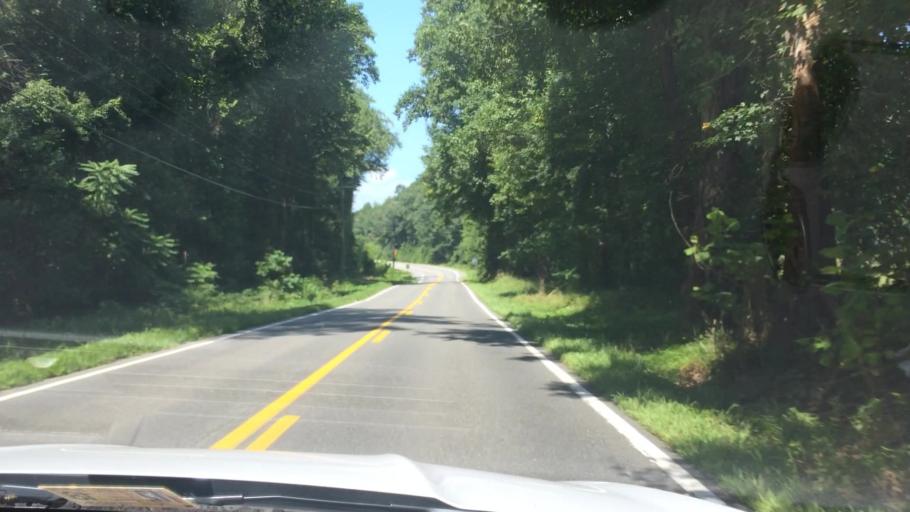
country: US
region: Virginia
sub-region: New Kent County
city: New Kent
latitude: 37.5244
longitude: -77.0699
